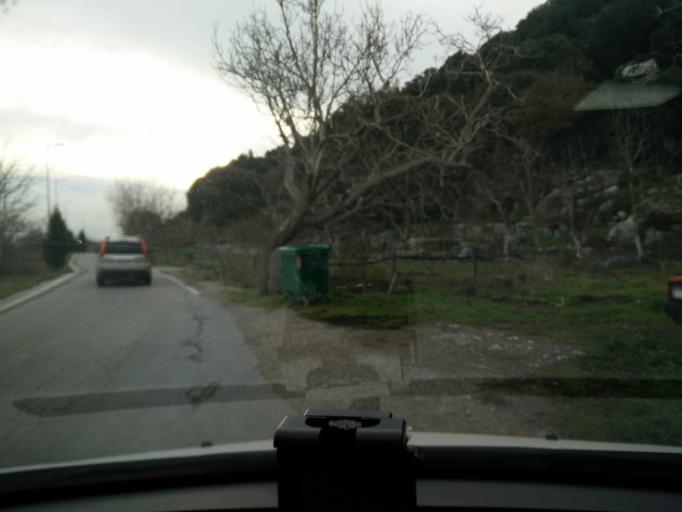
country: GR
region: Crete
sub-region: Nomos Irakleiou
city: Mokhos
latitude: 35.1996
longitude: 25.4694
